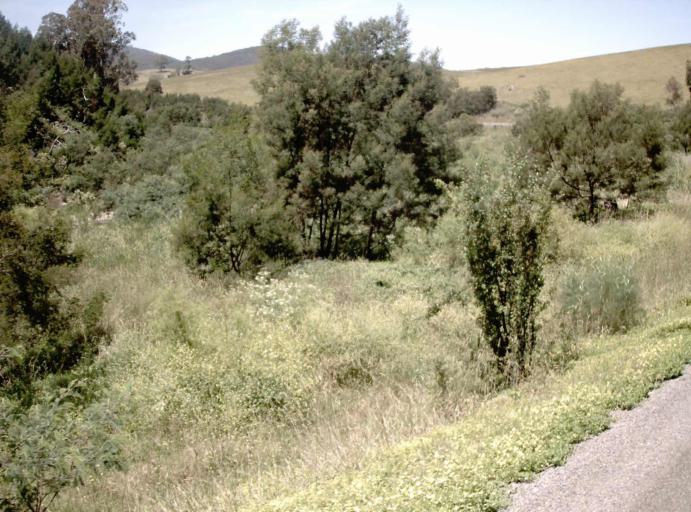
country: AU
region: Victoria
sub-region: East Gippsland
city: Bairnsdale
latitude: -37.4948
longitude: 147.8337
